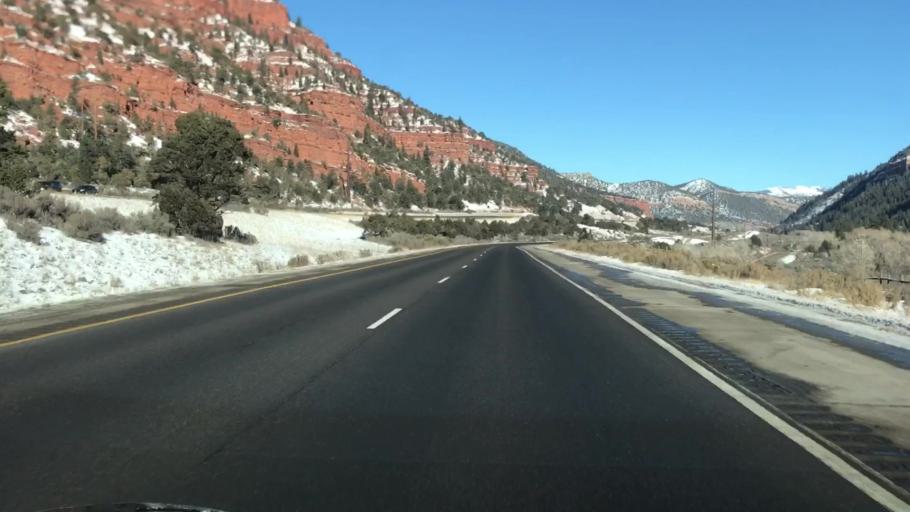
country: US
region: Colorado
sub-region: Eagle County
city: Eagle
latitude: 39.6922
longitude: -106.7471
